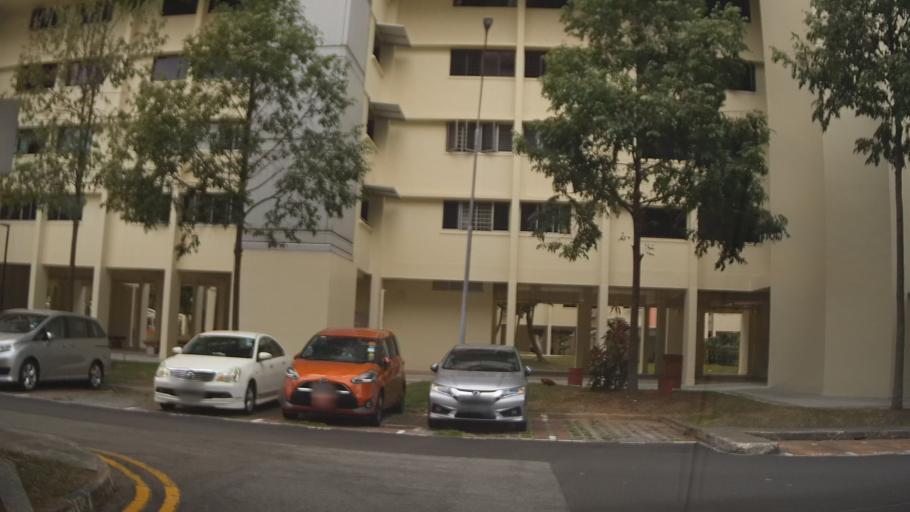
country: SG
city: Singapore
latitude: 1.3060
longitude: 103.7625
